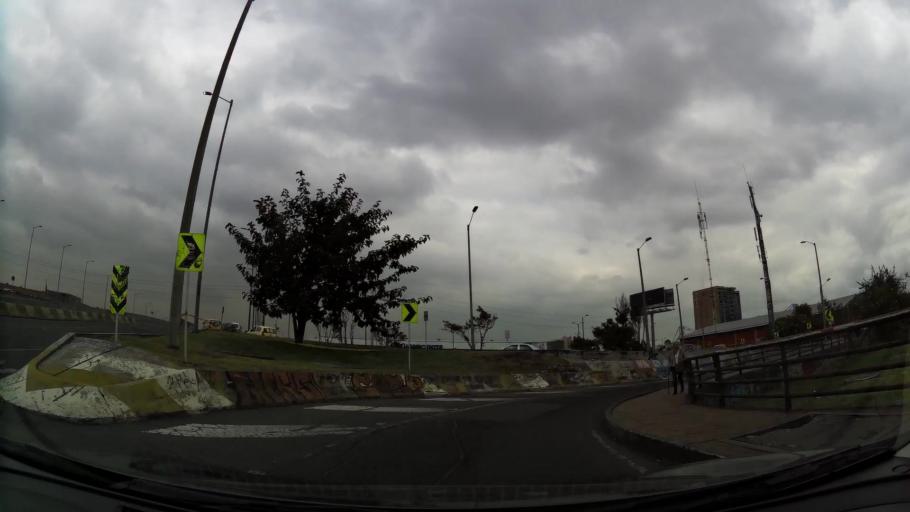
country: CO
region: Bogota D.C.
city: Barrio San Luis
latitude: 4.6833
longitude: -74.0783
